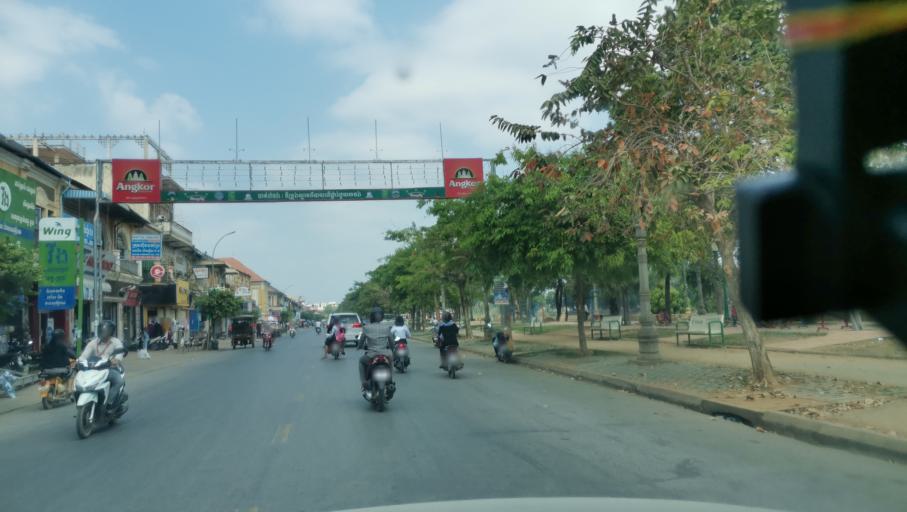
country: KH
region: Battambang
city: Battambang
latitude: 13.0989
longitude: 103.1991
